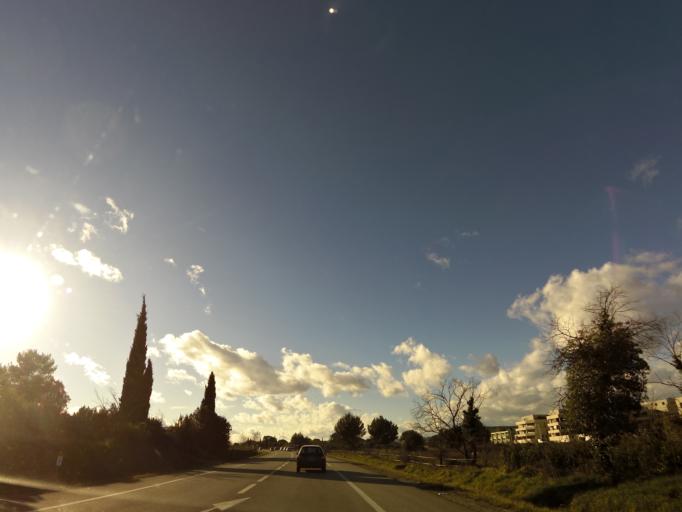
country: FR
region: Languedoc-Roussillon
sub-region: Departement du Gard
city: Caveirac
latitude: 43.8228
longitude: 4.2759
